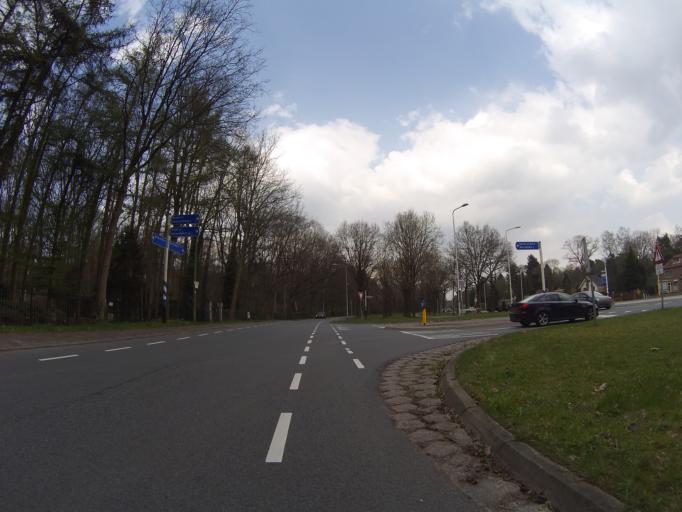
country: NL
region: Utrecht
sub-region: Gemeente Zeist
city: Zeist
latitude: 52.1289
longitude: 5.2491
